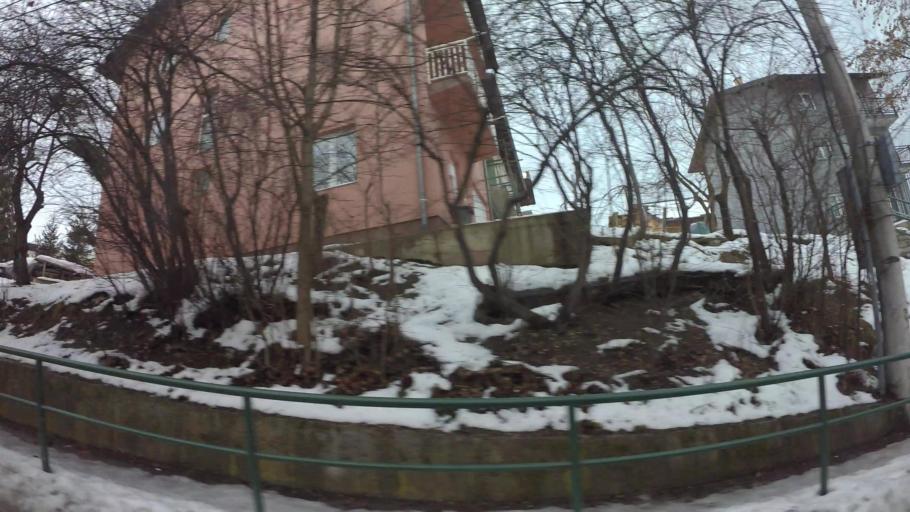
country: BA
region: Federation of Bosnia and Herzegovina
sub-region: Kanton Sarajevo
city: Sarajevo
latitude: 43.8600
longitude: 18.3637
